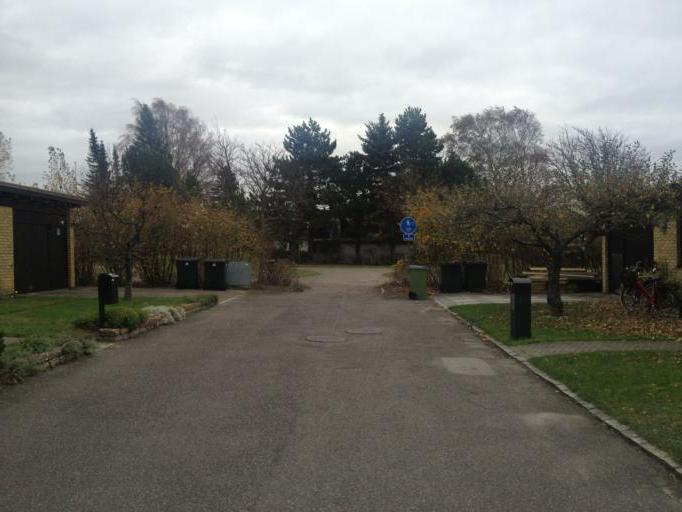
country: SE
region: Skane
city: Bjarred
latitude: 55.7235
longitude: 13.0258
